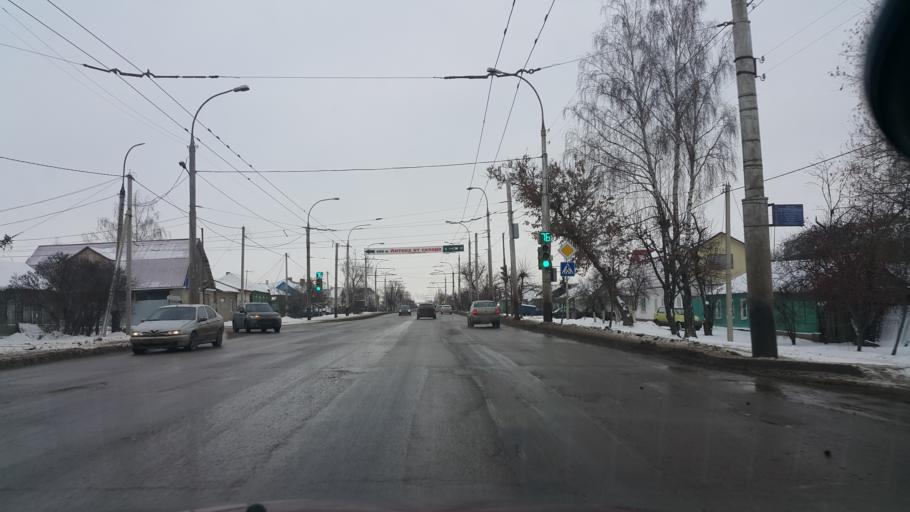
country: RU
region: Tambov
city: Tambov
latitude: 52.7240
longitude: 41.4035
